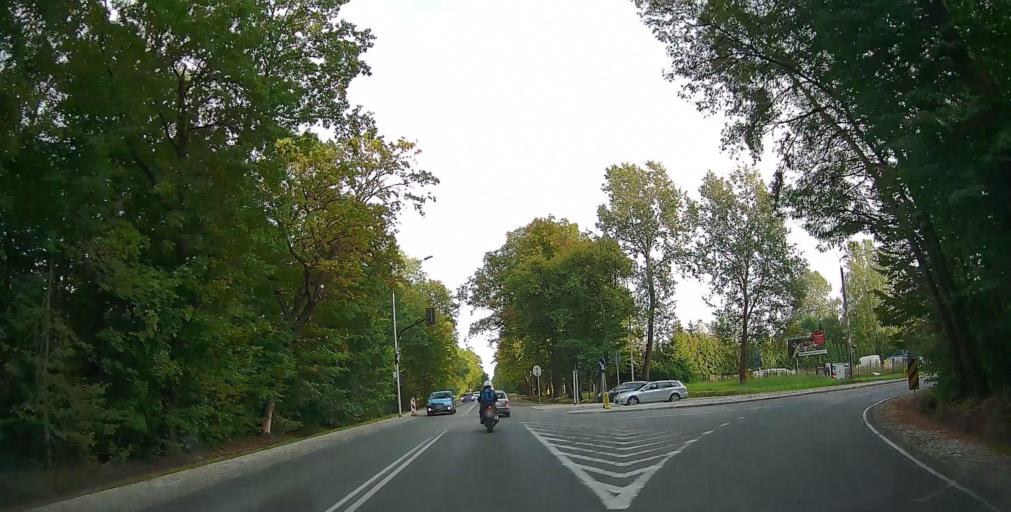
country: PL
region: Masovian Voivodeship
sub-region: Powiat piaseczynski
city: Zabieniec
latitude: 52.0434
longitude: 21.0810
